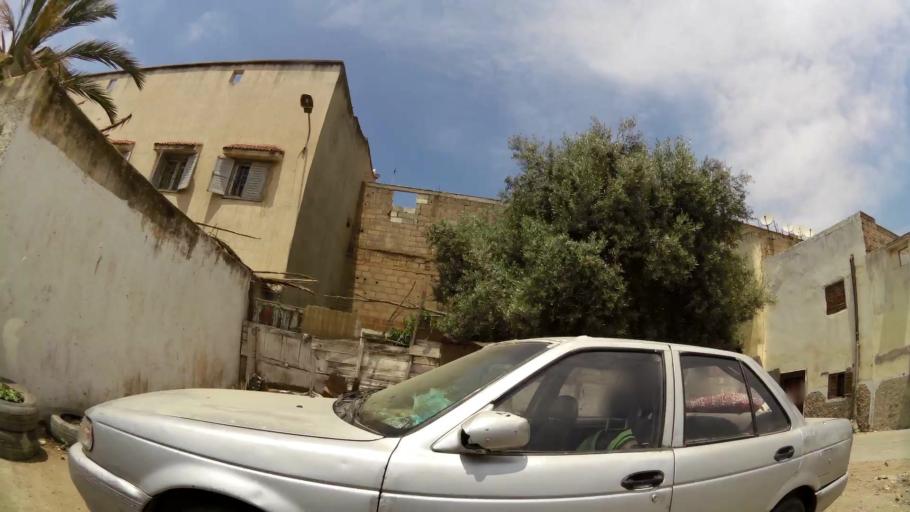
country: MA
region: Rabat-Sale-Zemmour-Zaer
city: Sale
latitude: 34.0514
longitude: -6.7893
